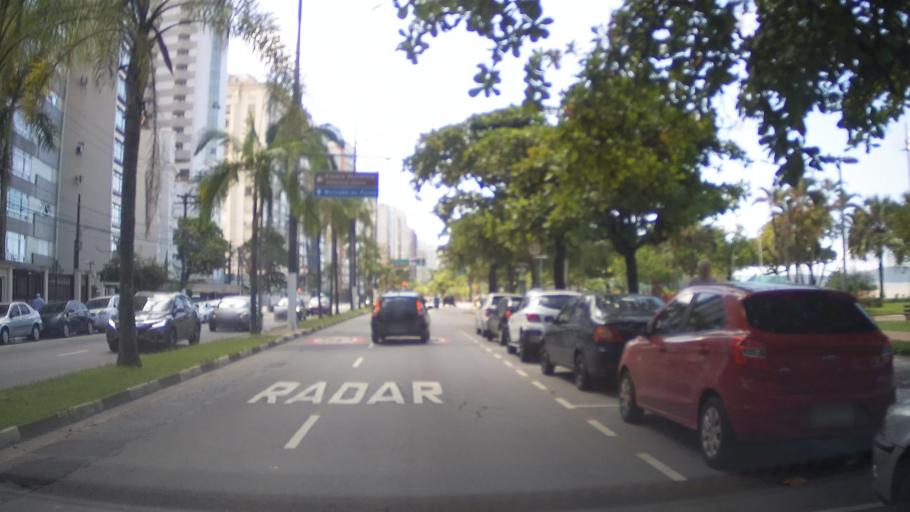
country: BR
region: Sao Paulo
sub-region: Santos
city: Santos
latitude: -23.9703
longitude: -46.3304
